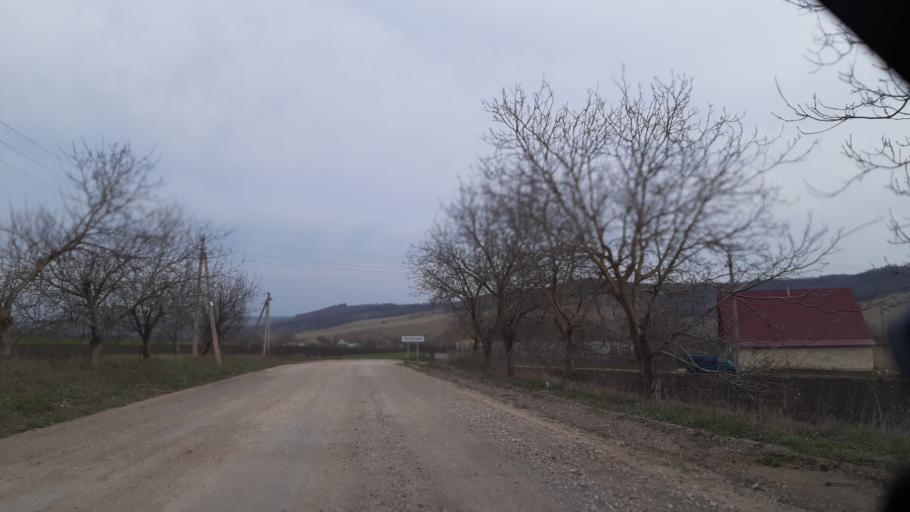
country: MD
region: Soldanesti
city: Soldanesti
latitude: 47.6891
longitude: 28.7435
